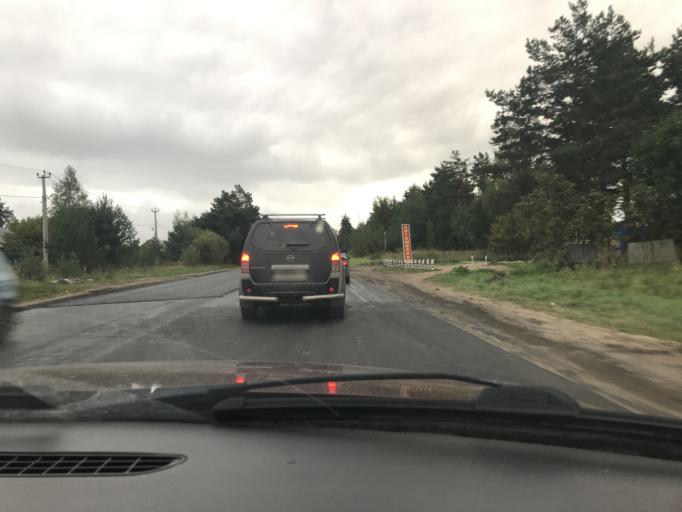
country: RU
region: Kaluga
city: Pyatovskiy
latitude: 54.6478
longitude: 36.0366
